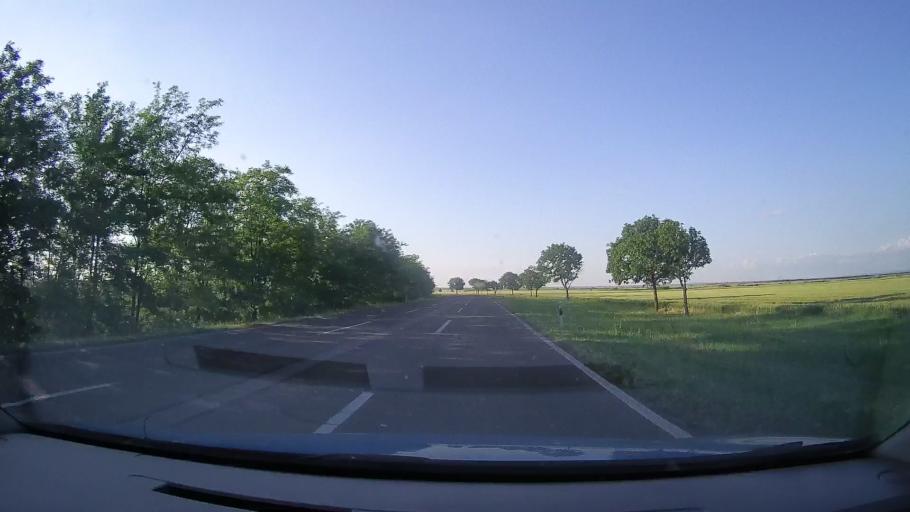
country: RO
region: Timis
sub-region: Comuna Moravita
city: Moravita
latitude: 45.2157
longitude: 21.2997
